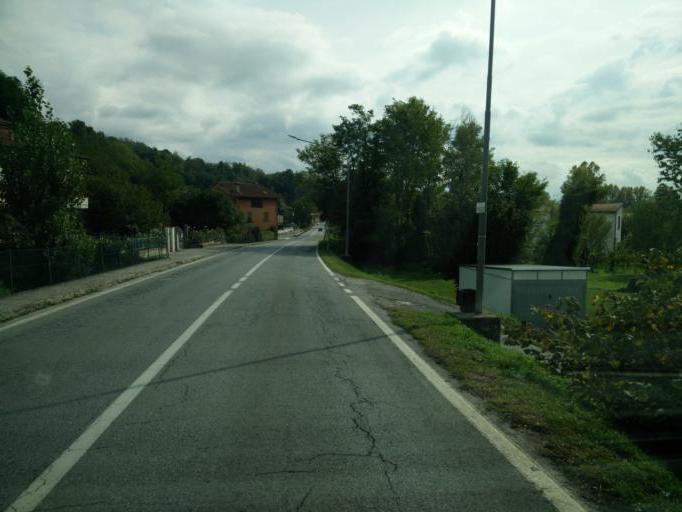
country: IT
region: Tuscany
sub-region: Provincia di Massa-Carrara
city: Filattiera
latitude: 44.3300
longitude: 9.9341
